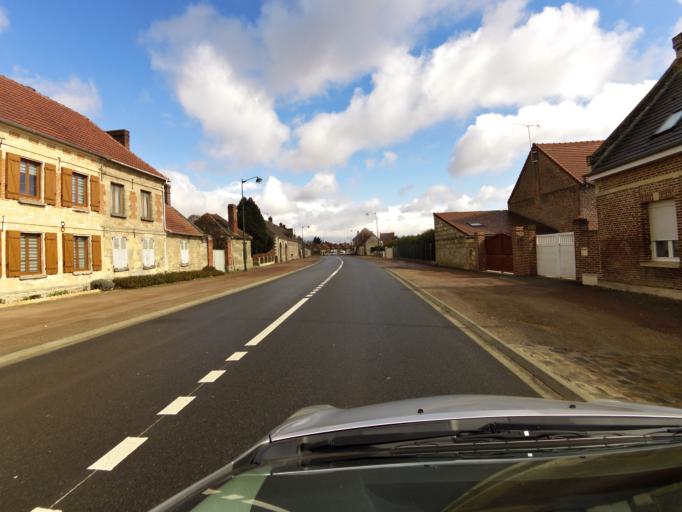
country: FR
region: Picardie
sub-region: Departement de l'Oise
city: Ressons-sur-Matz
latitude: 49.5743
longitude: 2.7045
